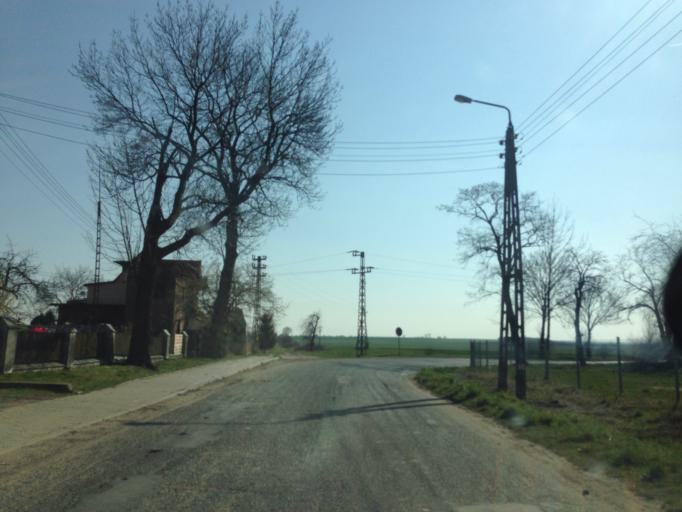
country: PL
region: Lower Silesian Voivodeship
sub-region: Powiat olesnicki
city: Bierutow
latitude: 51.1986
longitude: 17.5385
